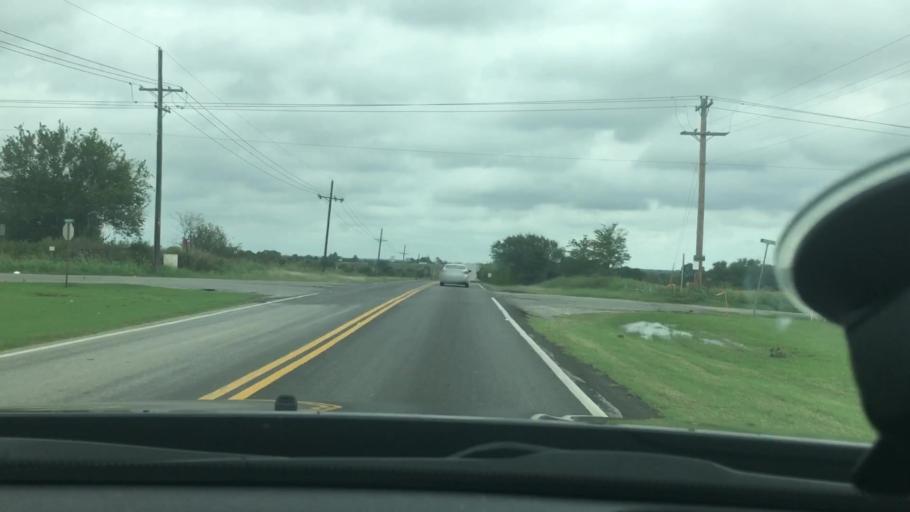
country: US
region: Oklahoma
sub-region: Bryan County
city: Durant
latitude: 33.9539
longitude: -96.3732
